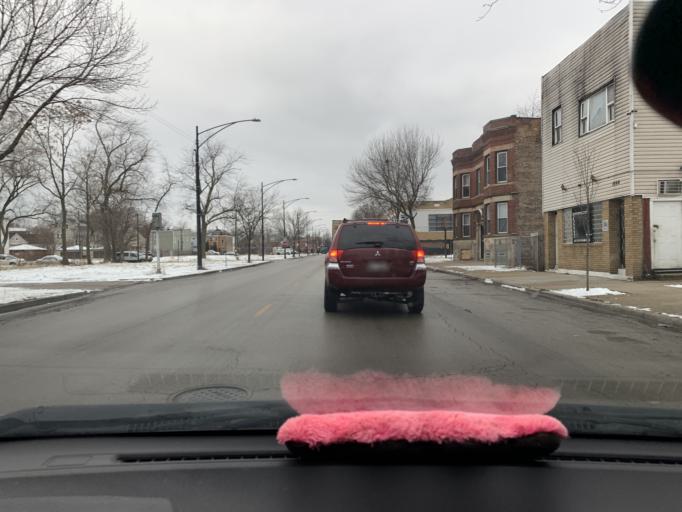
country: US
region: Illinois
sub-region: Cook County
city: Chicago
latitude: 41.8015
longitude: -87.6518
